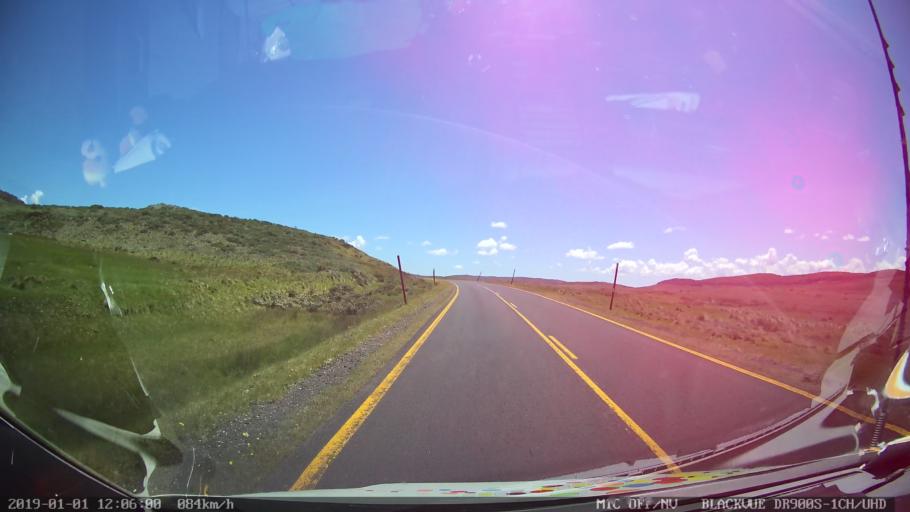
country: AU
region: New South Wales
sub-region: Snowy River
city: Jindabyne
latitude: -35.8502
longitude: 148.4909
